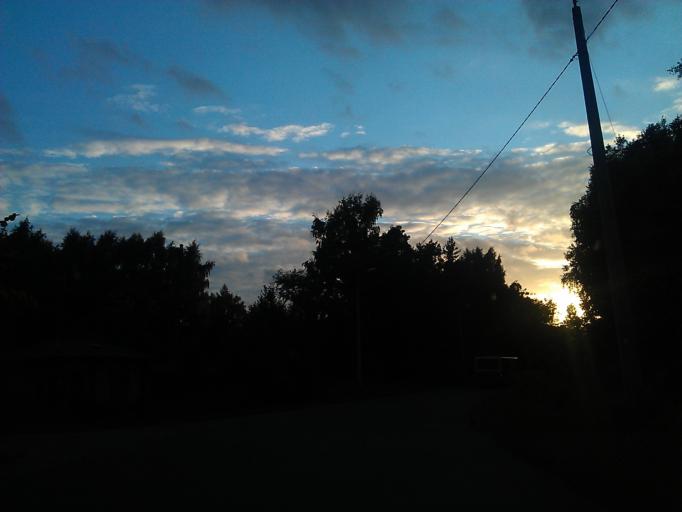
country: LV
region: Riga
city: Bergi
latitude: 56.9728
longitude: 24.2601
